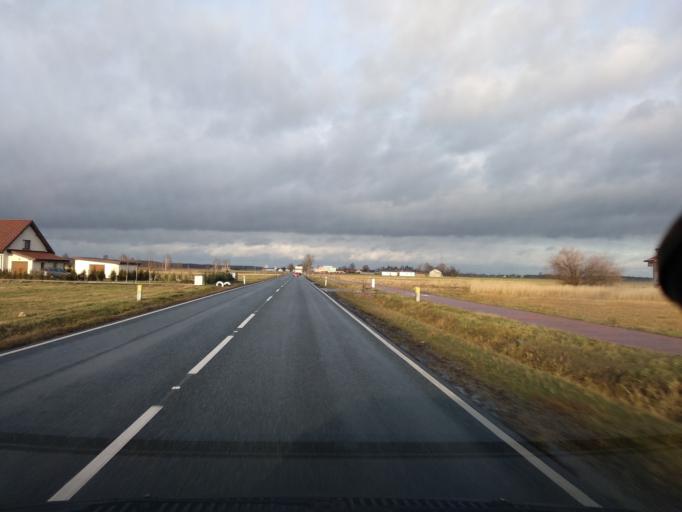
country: PL
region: Greater Poland Voivodeship
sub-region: Powiat koninski
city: Rychwal
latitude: 52.1050
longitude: 18.1674
